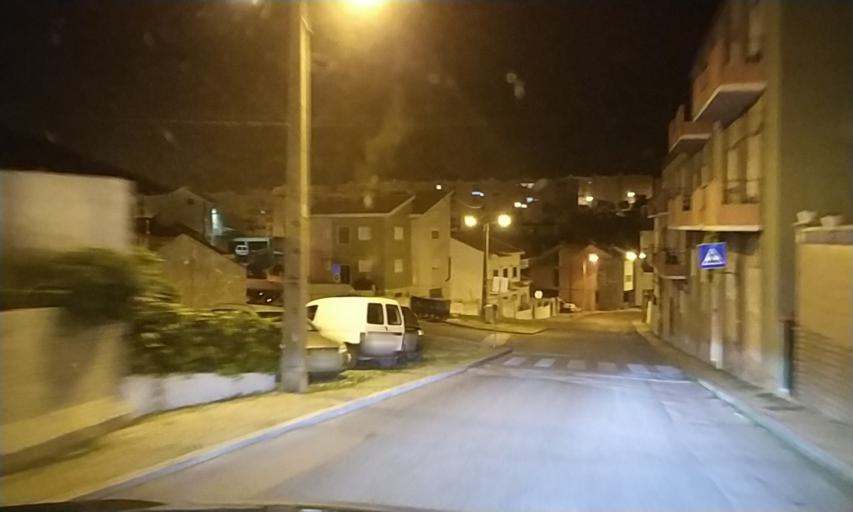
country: PT
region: Setubal
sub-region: Setubal
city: Setubal
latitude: 38.5258
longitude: -8.9105
